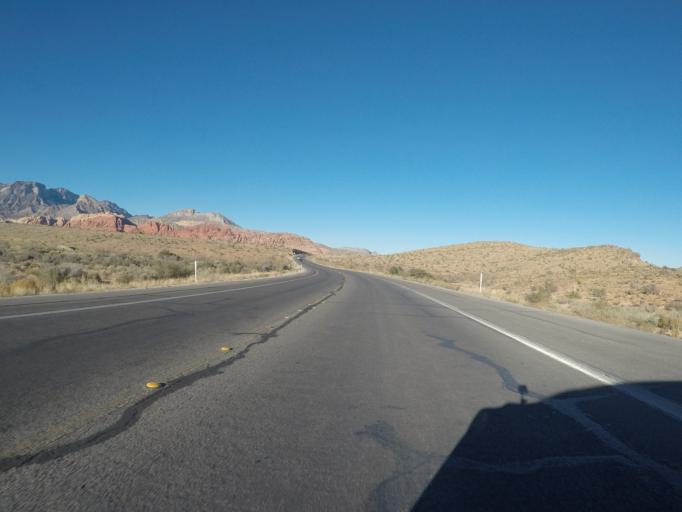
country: US
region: Nevada
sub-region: Clark County
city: Summerlin South
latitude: 36.1218
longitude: -115.4339
